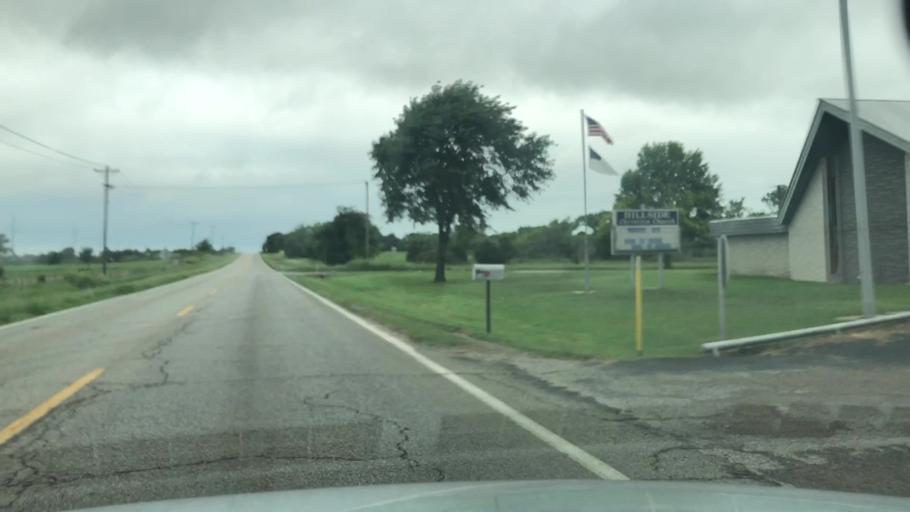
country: US
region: Oklahoma
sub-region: Nowata County
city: Nowata
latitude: 36.7067
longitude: -95.6539
